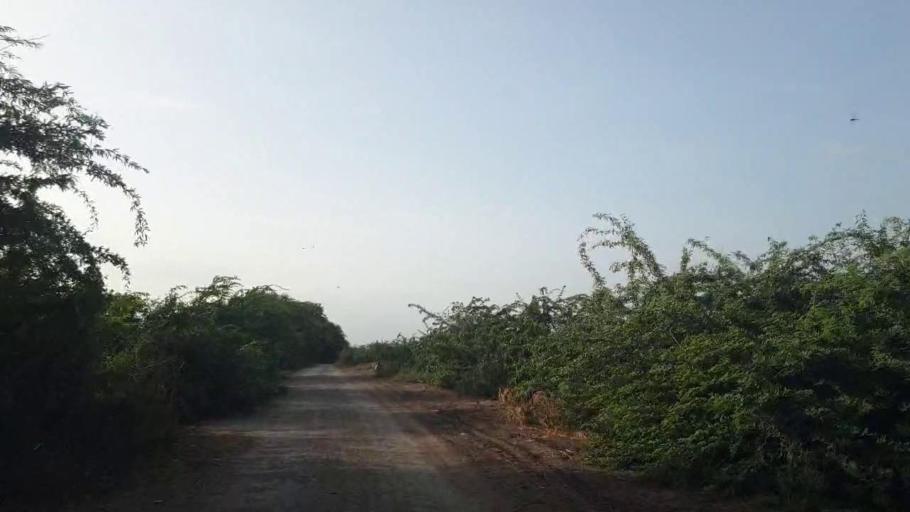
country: PK
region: Sindh
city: Kadhan
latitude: 24.6341
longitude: 69.1580
